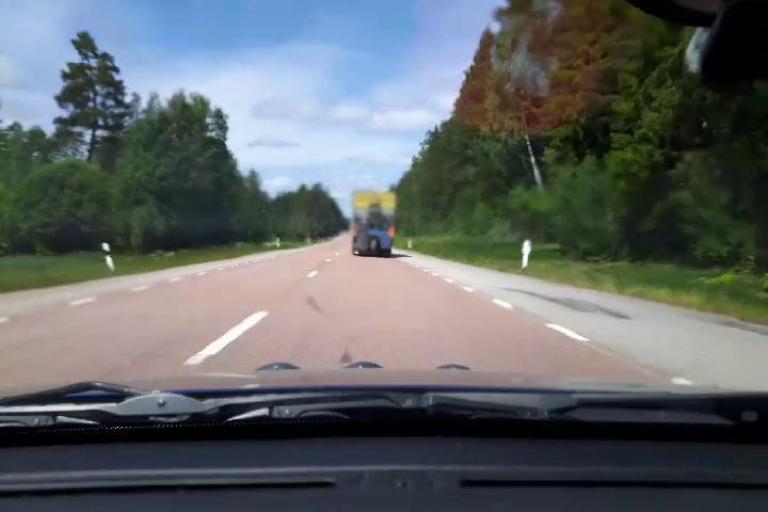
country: SE
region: Uppsala
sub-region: Osthammars Kommun
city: Bjorklinge
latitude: 60.1343
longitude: 17.5080
